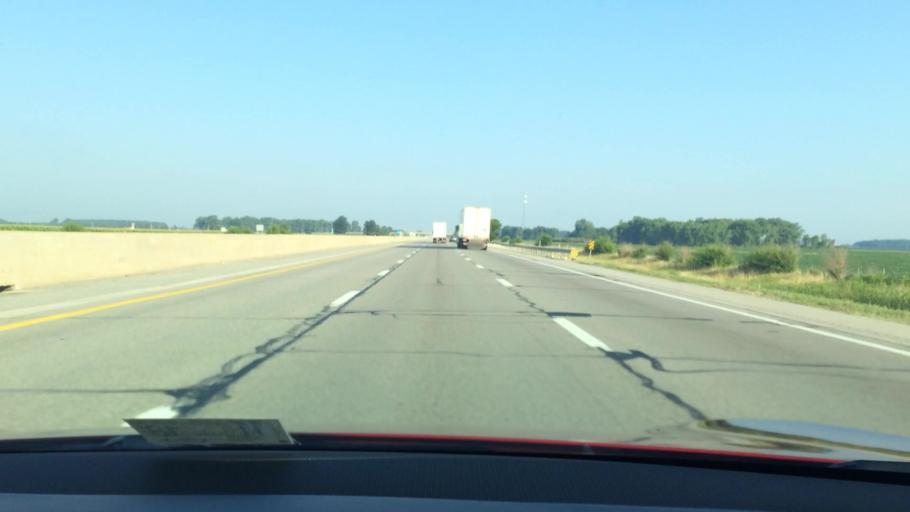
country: US
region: Ohio
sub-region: Sandusky County
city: Stony Prairie
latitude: 41.4315
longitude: -83.2065
